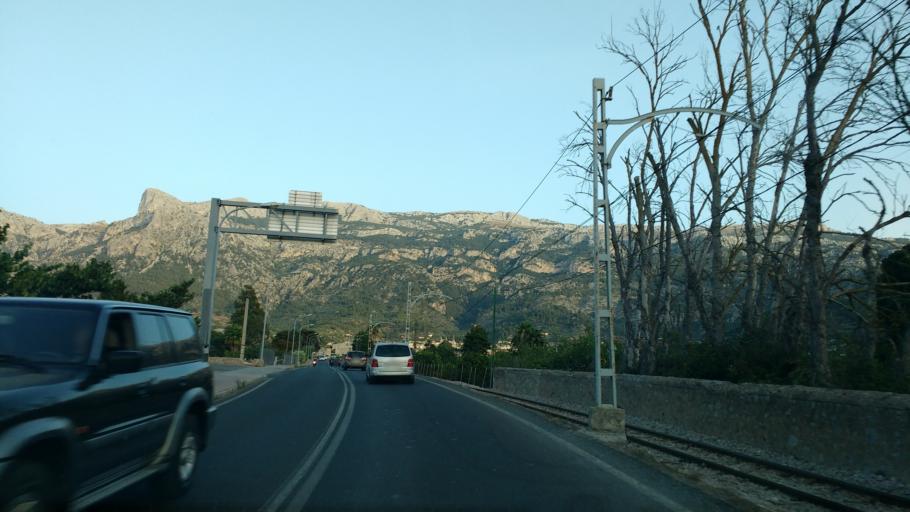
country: ES
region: Balearic Islands
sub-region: Illes Balears
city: Soller
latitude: 39.7807
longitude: 2.7012
